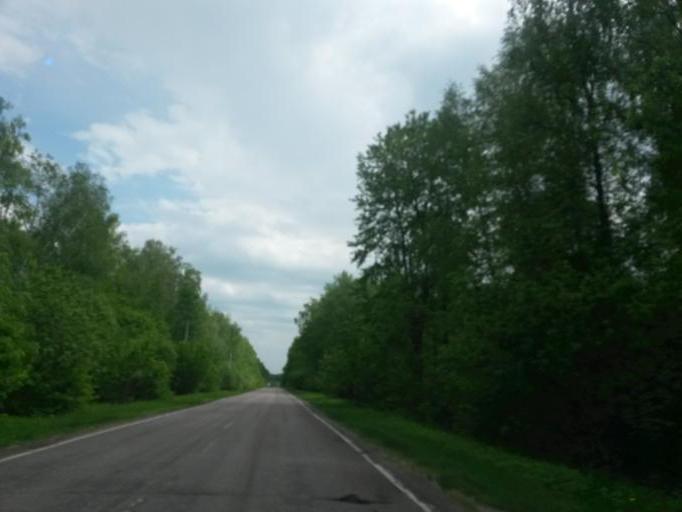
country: RU
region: Moskovskaya
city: Melikhovo
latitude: 55.2227
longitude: 37.6650
